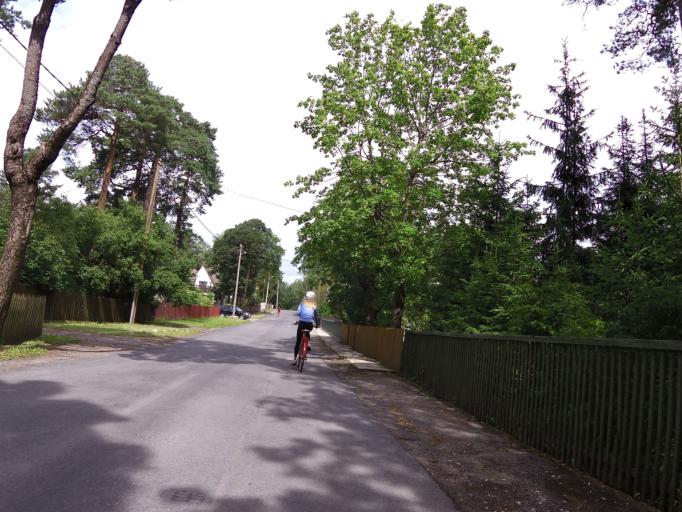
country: EE
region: Harju
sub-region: Saue vald
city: Laagri
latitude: 59.3860
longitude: 24.6670
